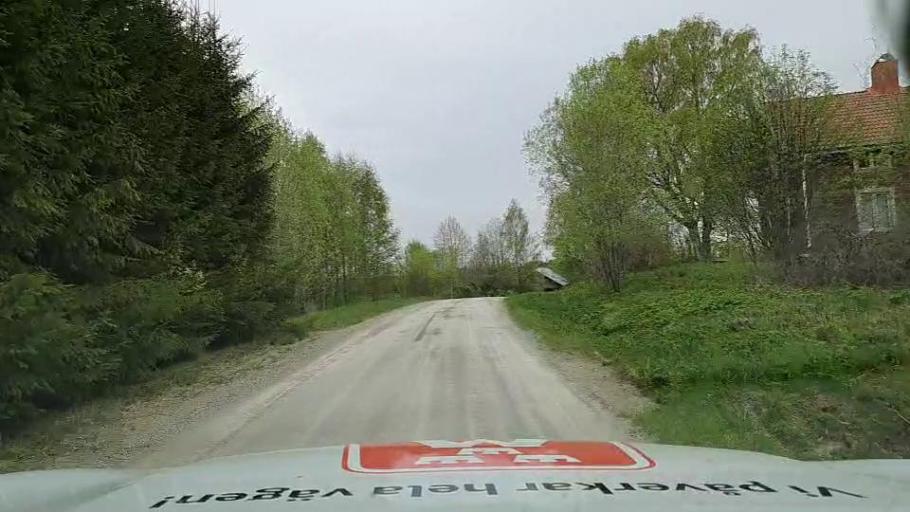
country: SE
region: Jaemtland
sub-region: Bergs Kommun
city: Hoverberg
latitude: 62.6818
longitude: 14.7735
